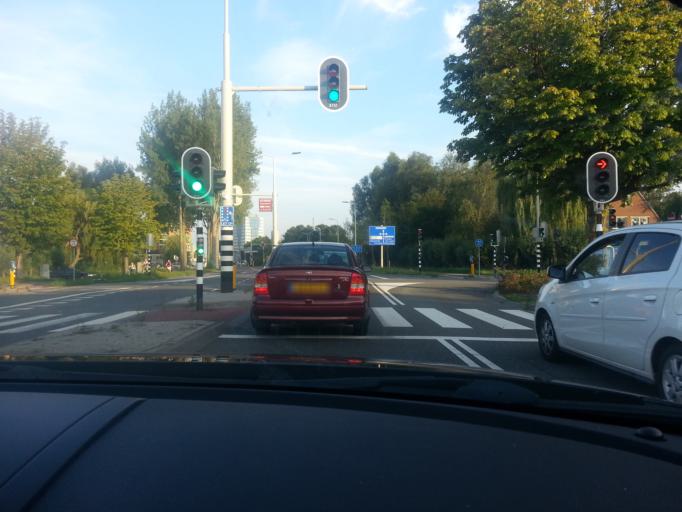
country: NL
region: South Holland
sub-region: Gemeente Capelle aan den IJssel
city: Capelle aan den IJssel
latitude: 51.9348
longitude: 4.5823
